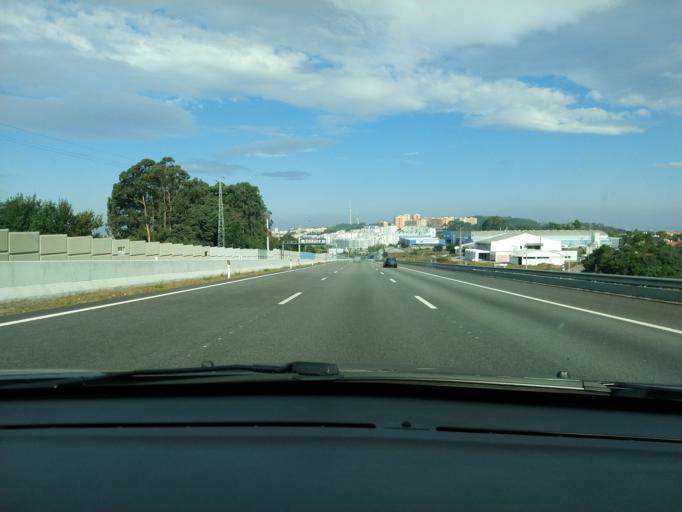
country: PT
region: Porto
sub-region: Vila Nova de Gaia
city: Canelas
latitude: 41.0854
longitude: -8.5844
